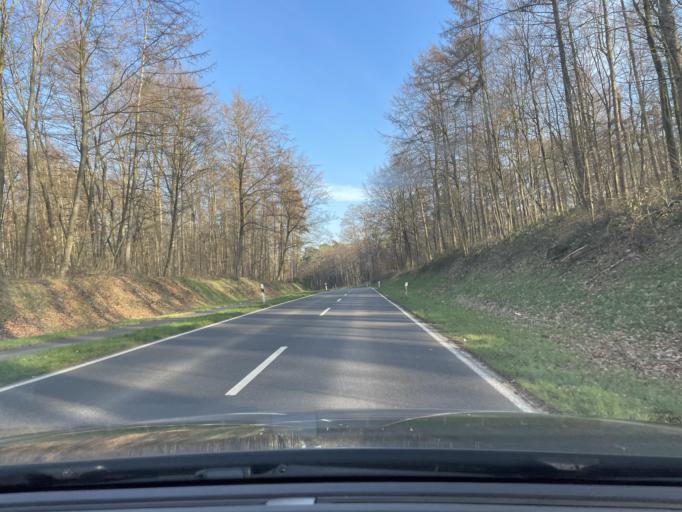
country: DE
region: North Rhine-Westphalia
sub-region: Regierungsbezirk Dusseldorf
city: Bruggen
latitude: 51.2333
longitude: 6.1767
